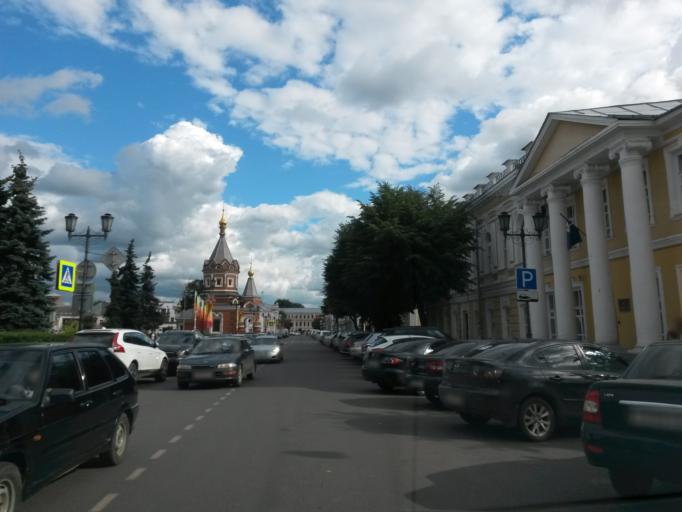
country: RU
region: Jaroslavl
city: Yaroslavl
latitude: 57.6261
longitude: 39.8898
